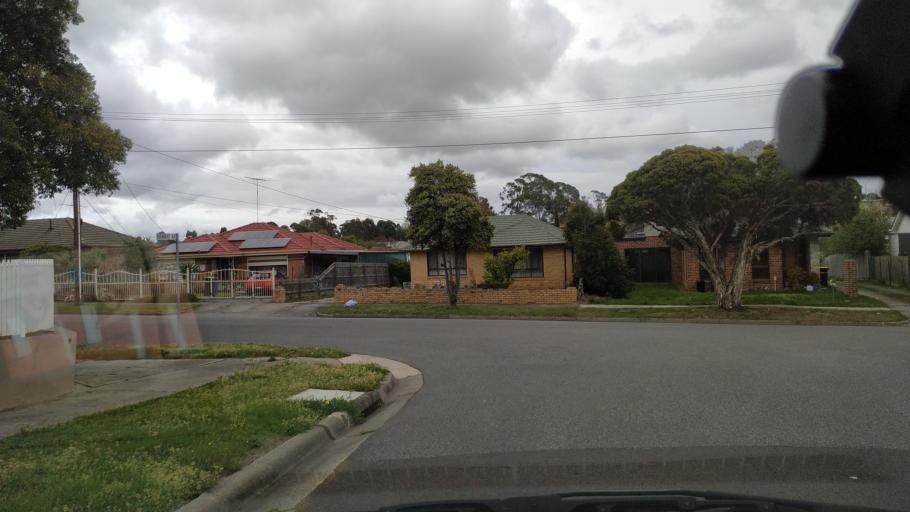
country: AU
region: Victoria
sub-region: Greater Dandenong
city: Noble Park North
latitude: -37.9627
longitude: 145.1942
